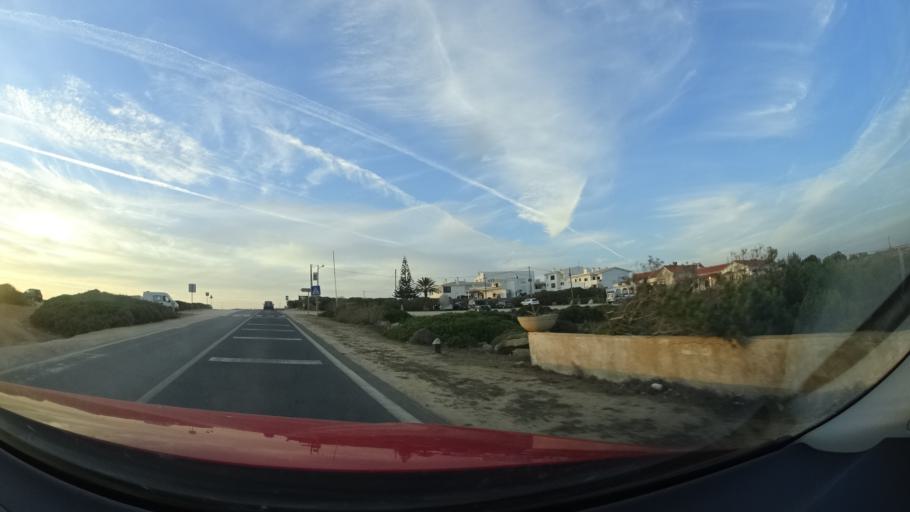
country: PT
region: Faro
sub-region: Vila do Bispo
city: Sagres
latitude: 37.0257
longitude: -8.9626
